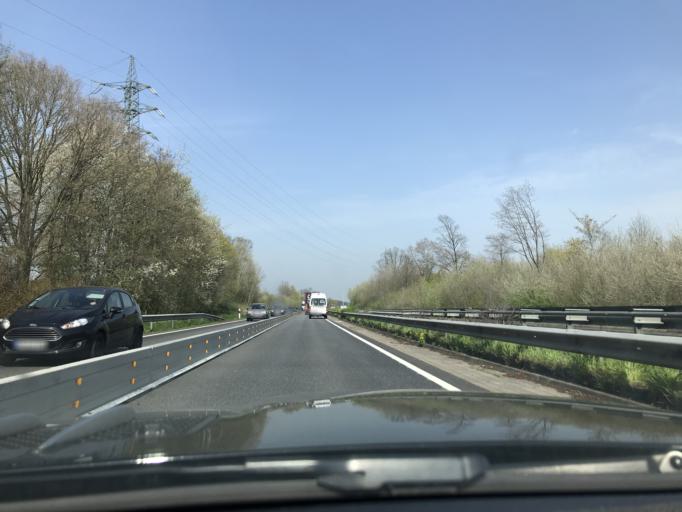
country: DE
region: Schleswig-Holstein
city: Neustadt in Holstein
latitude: 54.1078
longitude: 10.7821
